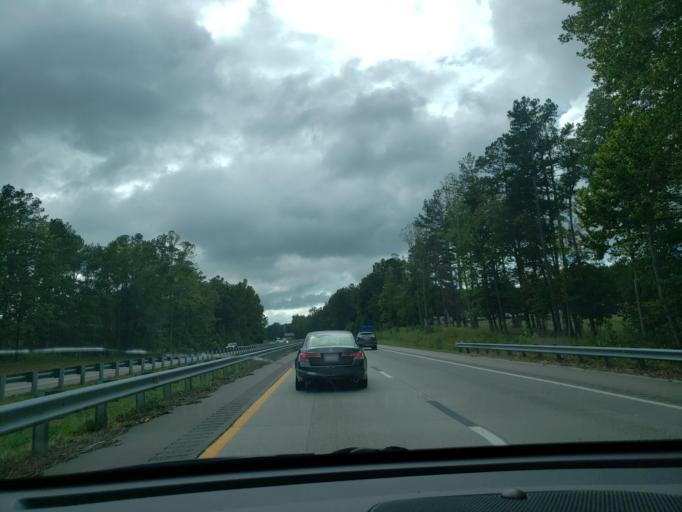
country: US
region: North Carolina
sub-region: Vance County
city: Henderson
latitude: 36.4152
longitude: -78.3182
